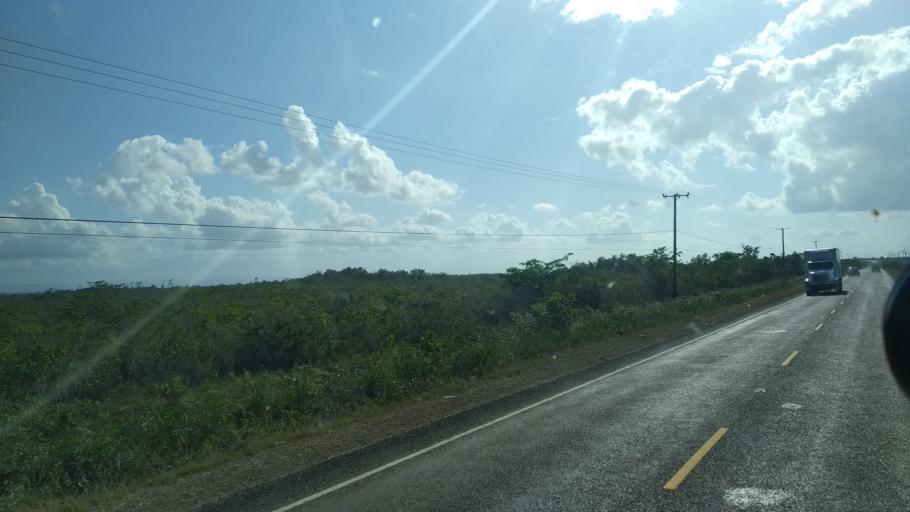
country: BZ
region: Belize
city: Belize City
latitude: 17.4058
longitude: -88.4880
